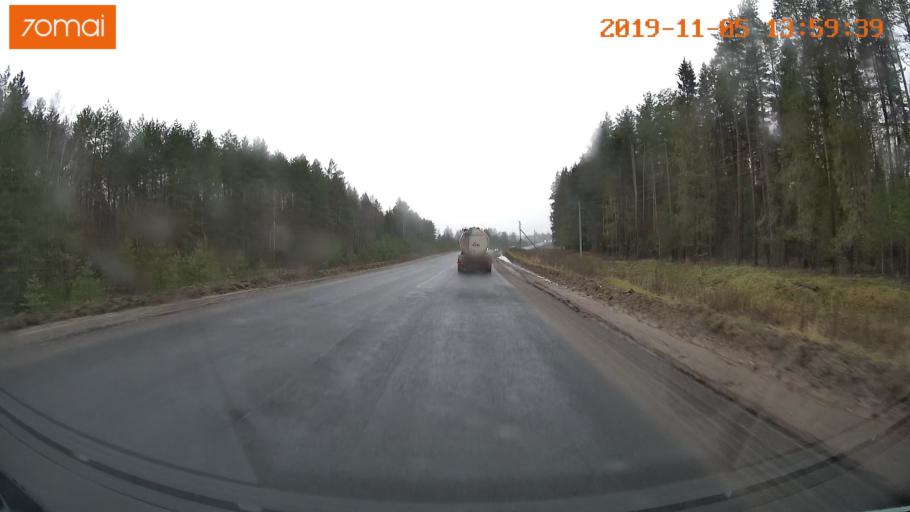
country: RU
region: Ivanovo
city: Kitovo
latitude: 57.0169
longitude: 41.2642
